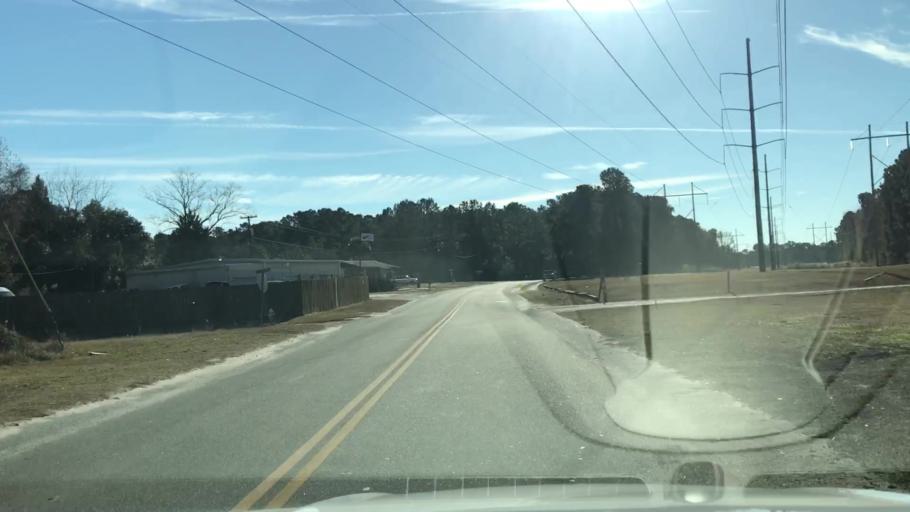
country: US
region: South Carolina
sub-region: Berkeley County
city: Ladson
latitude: 32.9944
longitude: -80.0969
